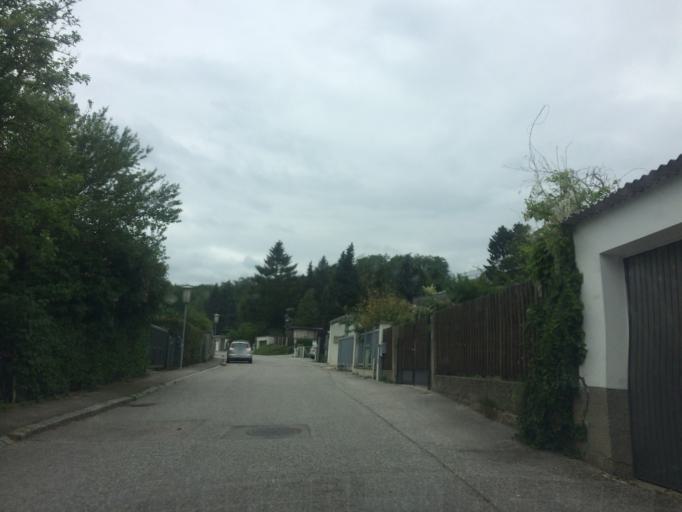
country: AT
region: Lower Austria
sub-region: Politischer Bezirk Wien-Umgebung
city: Gablitz
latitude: 48.2360
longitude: 16.1355
